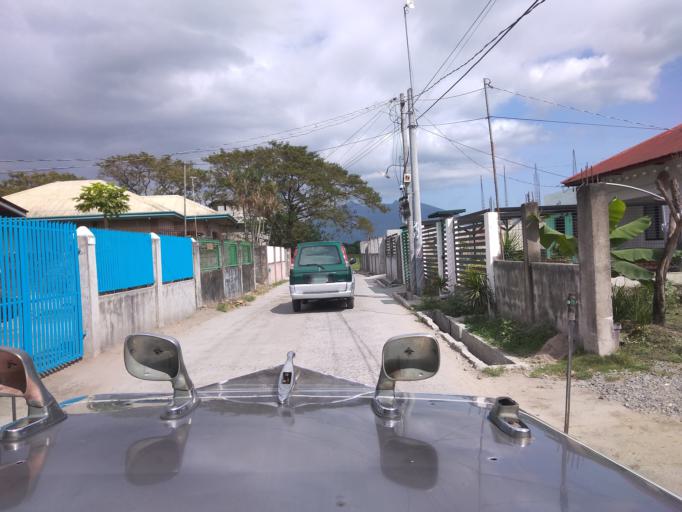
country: PH
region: Central Luzon
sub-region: Province of Pampanga
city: Pandacaqui
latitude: 15.1840
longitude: 120.6468
